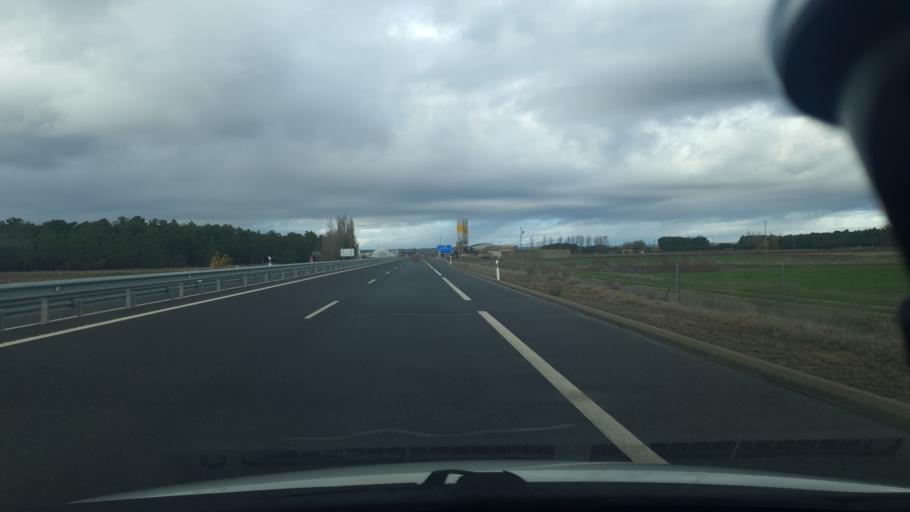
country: ES
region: Castille and Leon
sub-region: Provincia de Segovia
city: Sanchonuno
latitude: 41.3042
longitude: -4.3021
